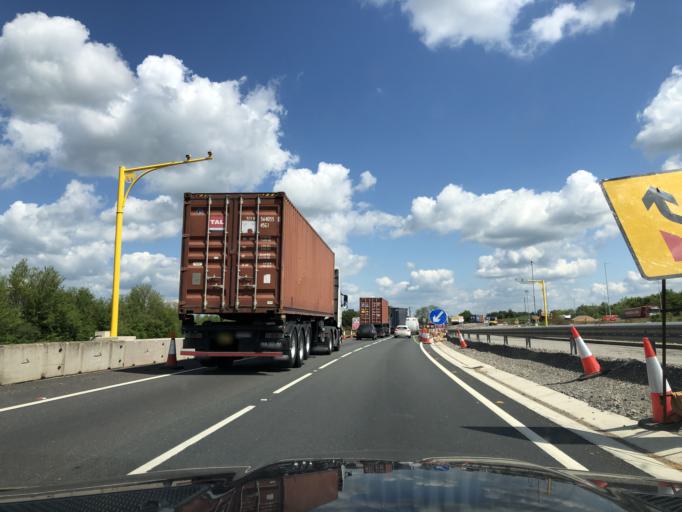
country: GB
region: England
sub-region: Cambridgeshire
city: Brampton
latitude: 52.3333
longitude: -0.2557
